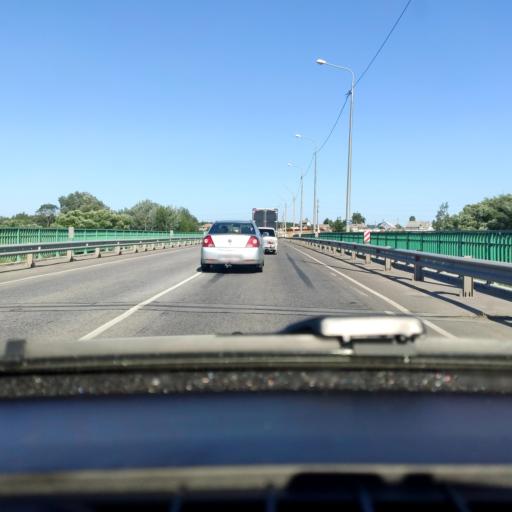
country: RU
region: Voronezj
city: Sadovoye
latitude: 51.4908
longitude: 40.4811
